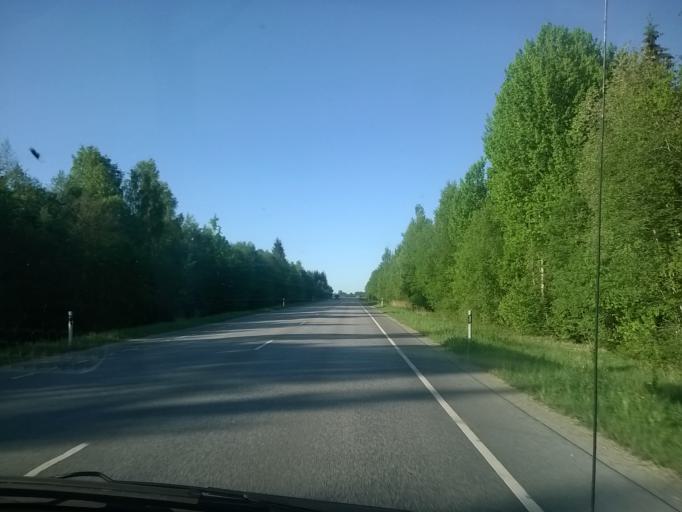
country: EE
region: Tartu
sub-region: Elva linn
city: Elva
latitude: 58.2076
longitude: 26.3595
